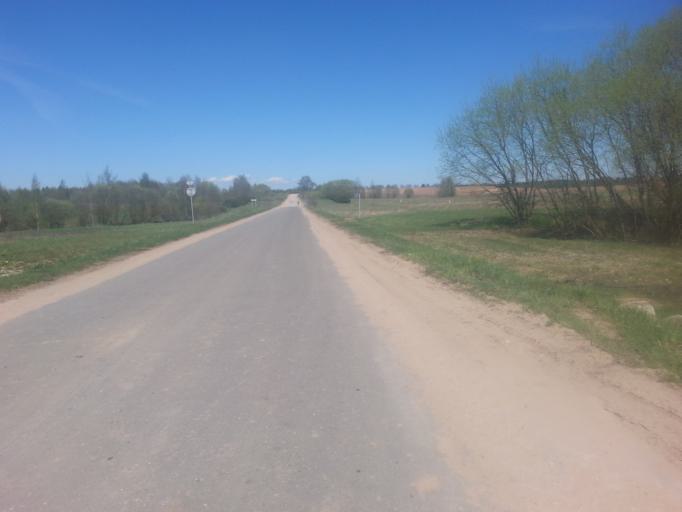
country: BY
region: Minsk
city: Narach
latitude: 54.9453
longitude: 26.6961
